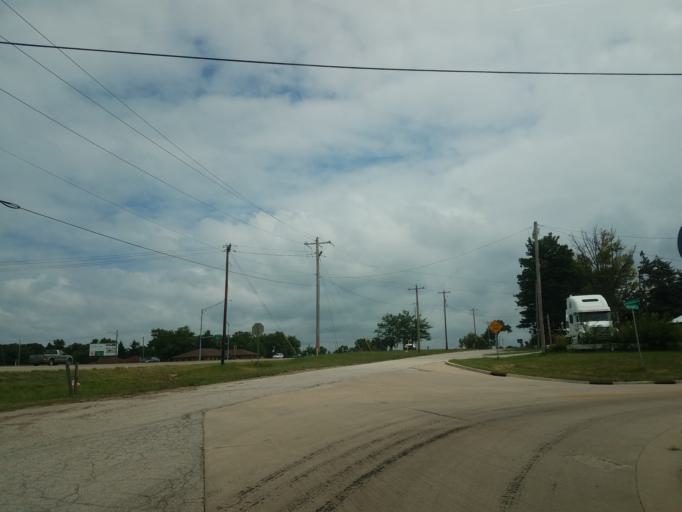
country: US
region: Illinois
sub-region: McLean County
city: Bloomington
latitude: 40.4487
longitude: -89.0153
